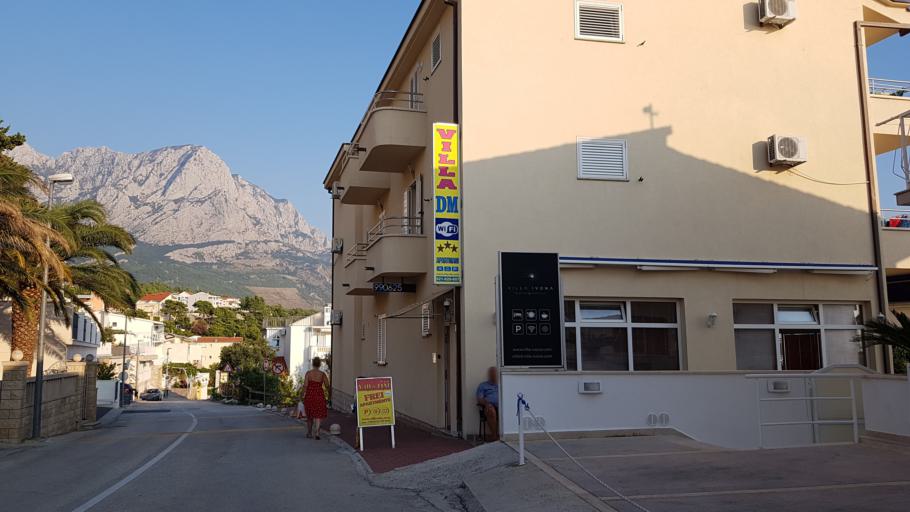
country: HR
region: Splitsko-Dalmatinska
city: Baska Voda
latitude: 43.3604
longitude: 16.9469
